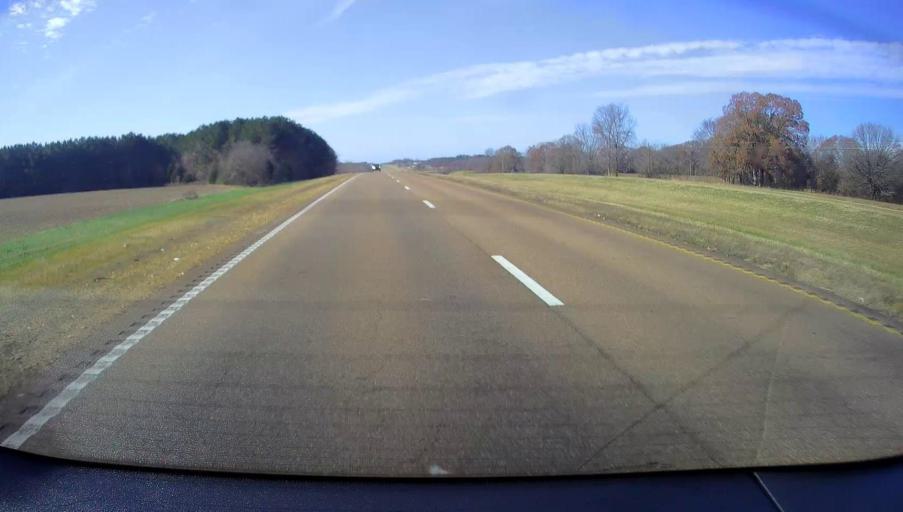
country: US
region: Mississippi
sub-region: Marshall County
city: Holly Springs
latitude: 34.9461
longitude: -89.3664
